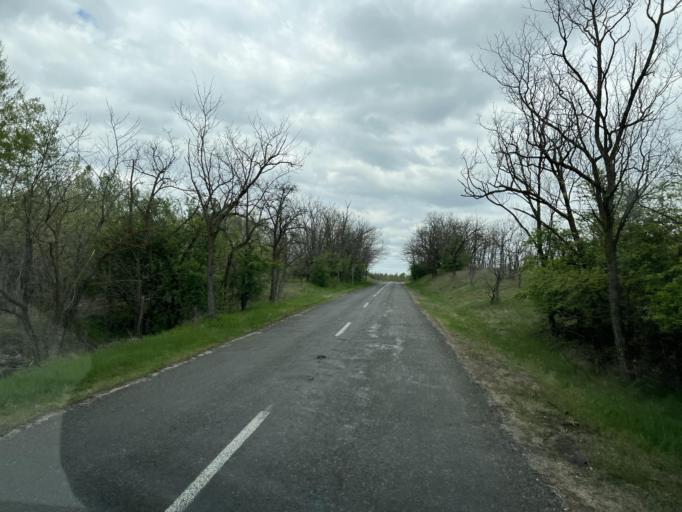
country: HU
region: Pest
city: Orkeny
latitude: 47.1148
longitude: 19.3582
